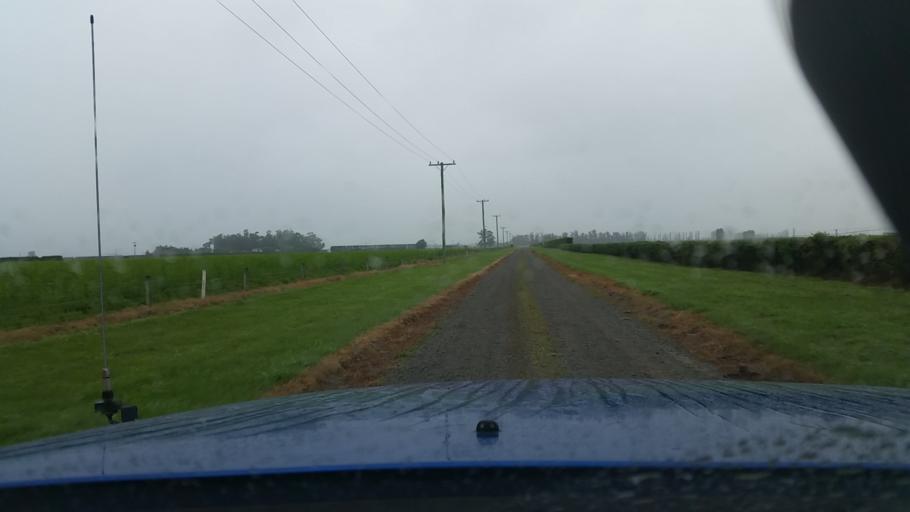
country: NZ
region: Canterbury
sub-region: Ashburton District
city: Tinwald
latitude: -44.0273
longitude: 171.7810
